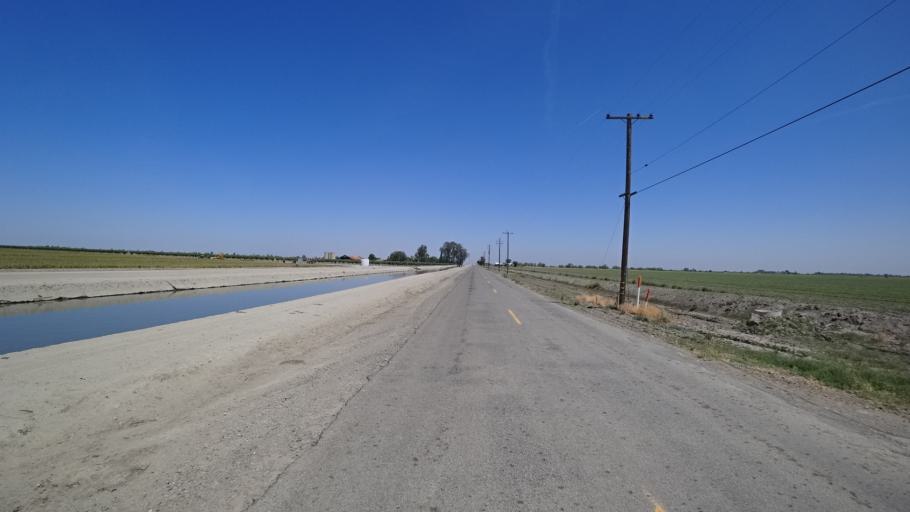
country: US
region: California
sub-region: Kings County
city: Corcoran
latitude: 36.0292
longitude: -119.5362
